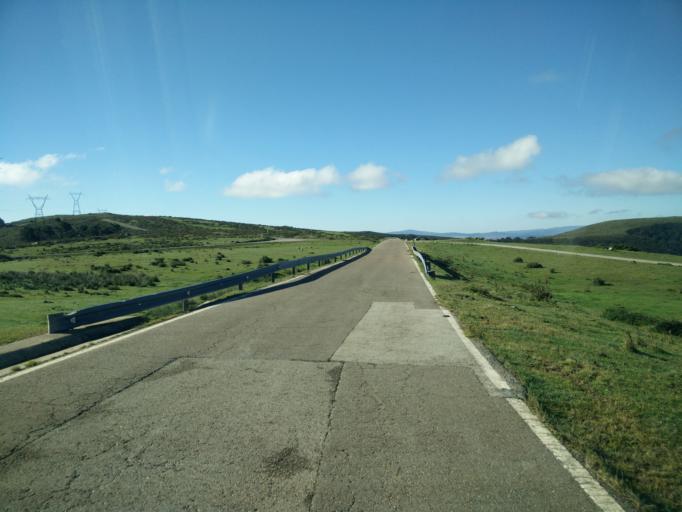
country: ES
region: Cantabria
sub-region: Provincia de Cantabria
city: San Pedro del Romeral
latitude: 43.0509
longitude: -3.8490
